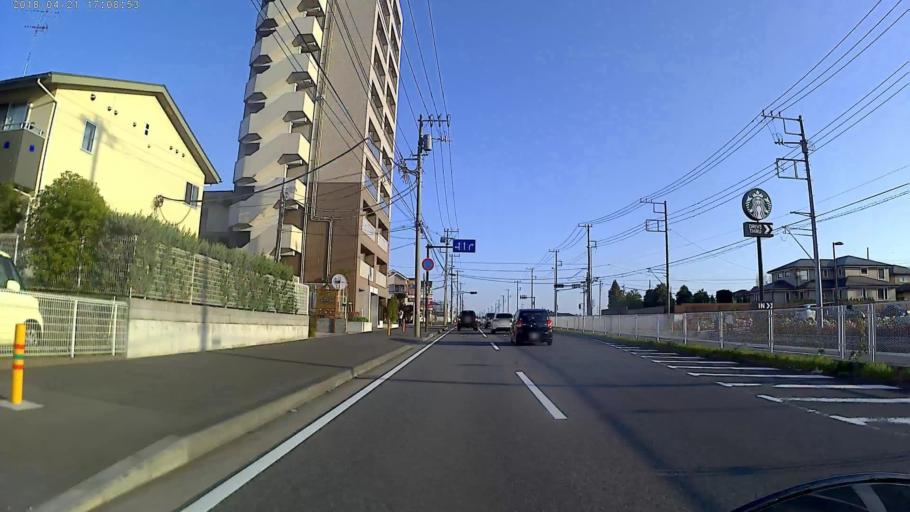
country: JP
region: Kanagawa
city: Fujisawa
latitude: 35.4027
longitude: 139.4417
